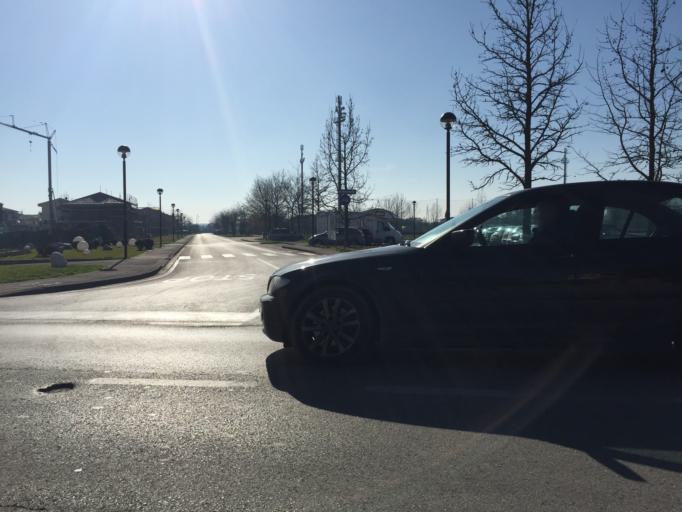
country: IT
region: Tuscany
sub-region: Provincia di Pistoia
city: Ponte Buggianese
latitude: 43.8397
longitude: 10.7459
